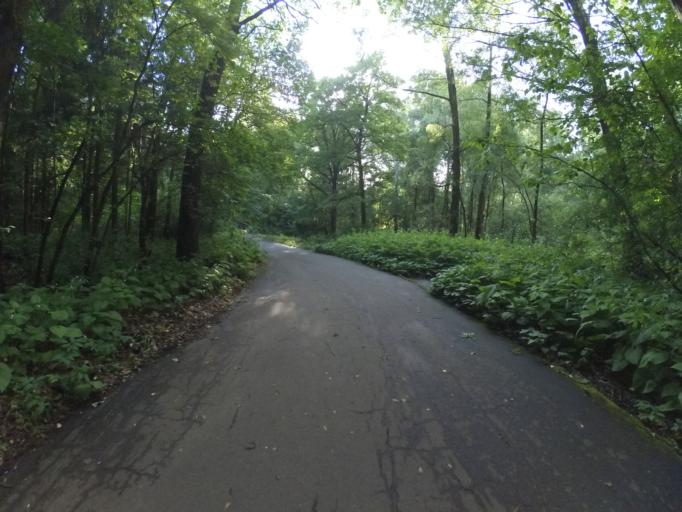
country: RU
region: Moscow
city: Ostankinskiy
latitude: 55.8413
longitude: 37.6127
